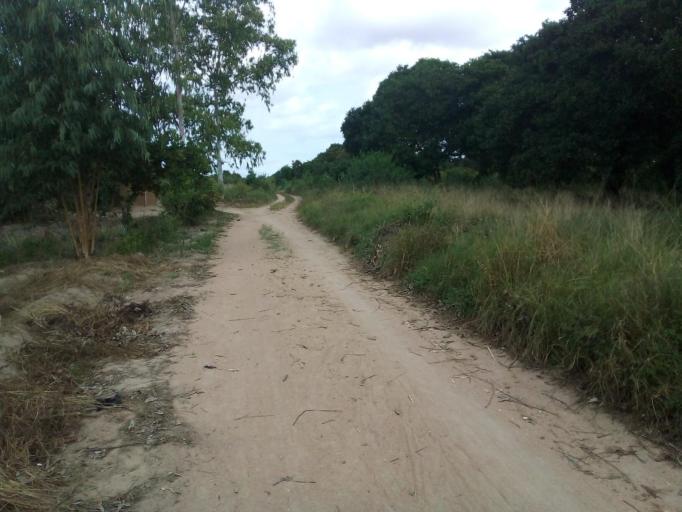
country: MZ
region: Zambezia
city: Quelimane
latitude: -17.5531
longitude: 36.7016
